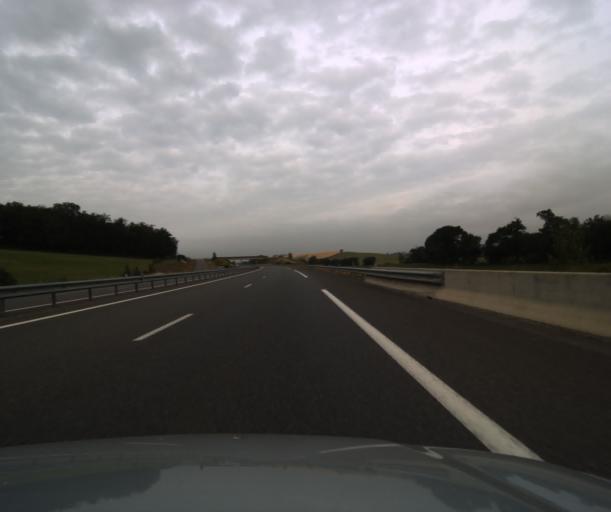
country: FR
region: Midi-Pyrenees
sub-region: Departement du Gers
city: Aubiet
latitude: 43.6600
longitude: 0.7684
